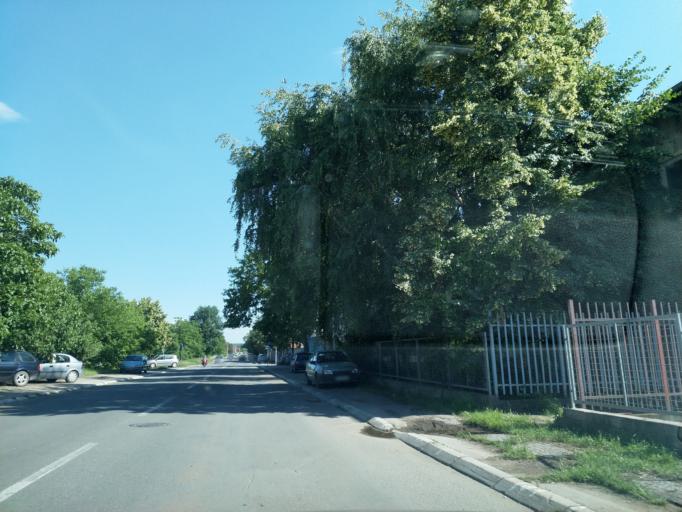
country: RS
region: Central Serbia
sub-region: Pomoravski Okrug
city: Paracin
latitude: 43.8558
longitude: 21.4071
